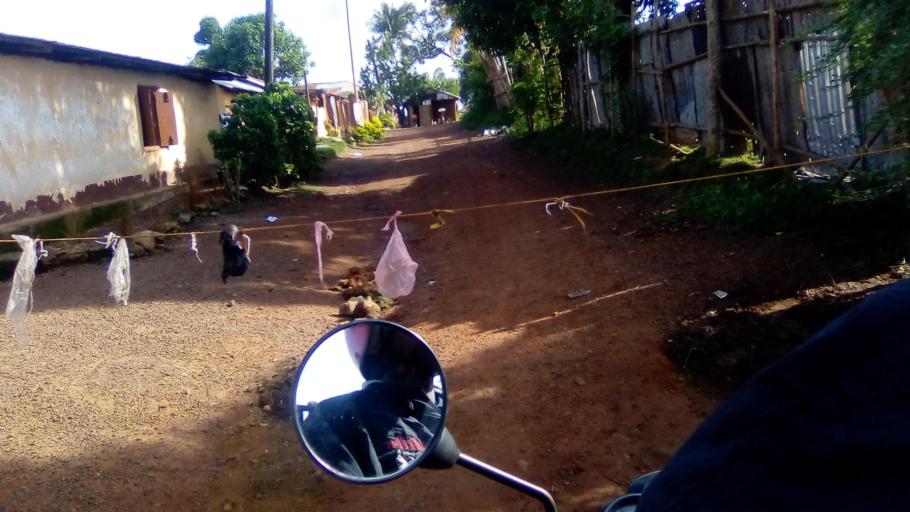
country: SL
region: Southern Province
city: Bo
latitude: 7.9546
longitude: -11.7579
